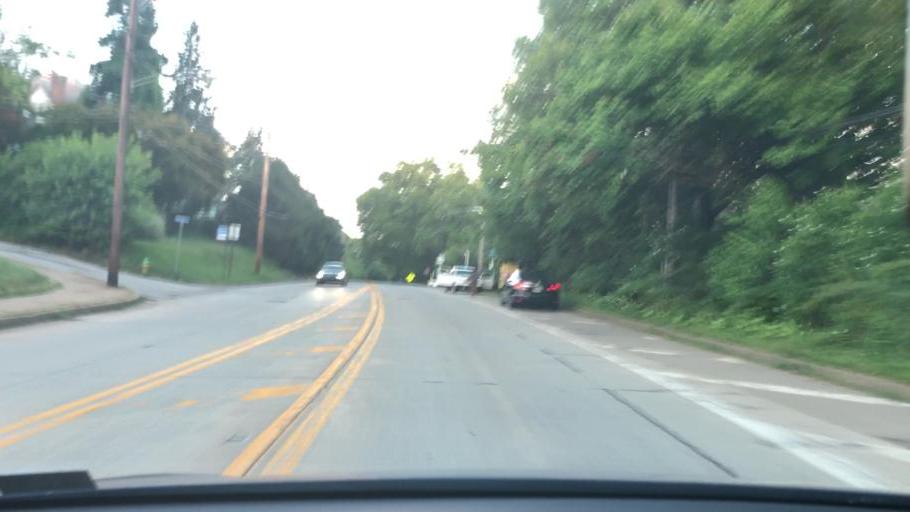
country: US
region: Pennsylvania
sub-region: Allegheny County
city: Wilkinsburg
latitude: 40.4615
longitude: -79.8614
